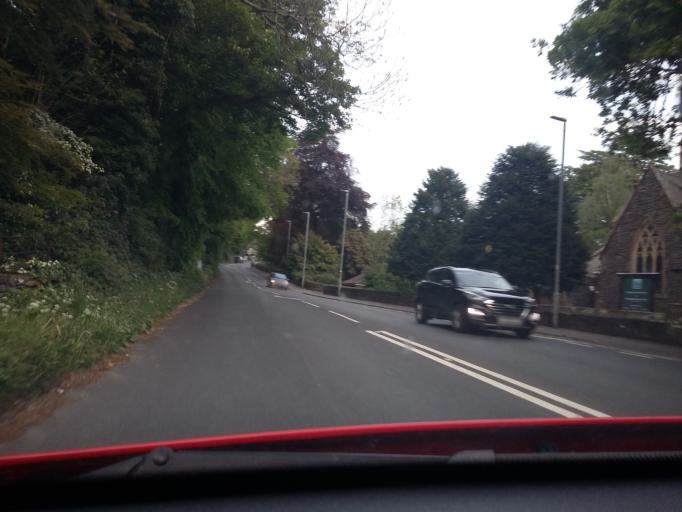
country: GB
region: England
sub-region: Cumbria
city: Windermere
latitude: 54.3813
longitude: -2.9103
